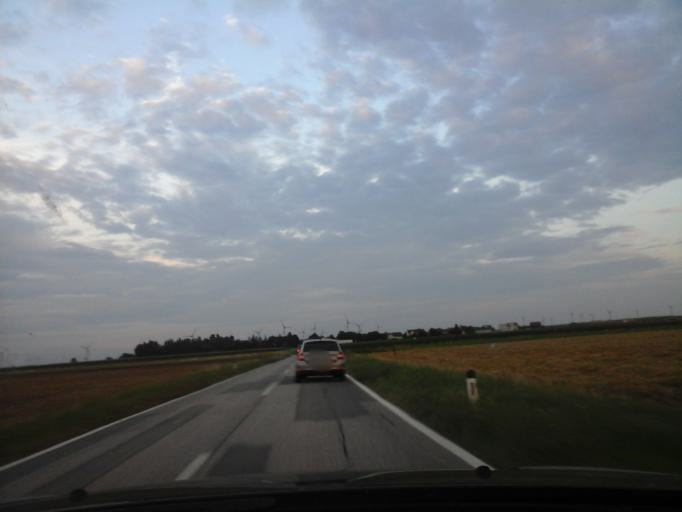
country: AT
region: Lower Austria
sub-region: Politischer Bezirk Bruck an der Leitha
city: Scharndorf
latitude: 48.1018
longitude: 16.7884
